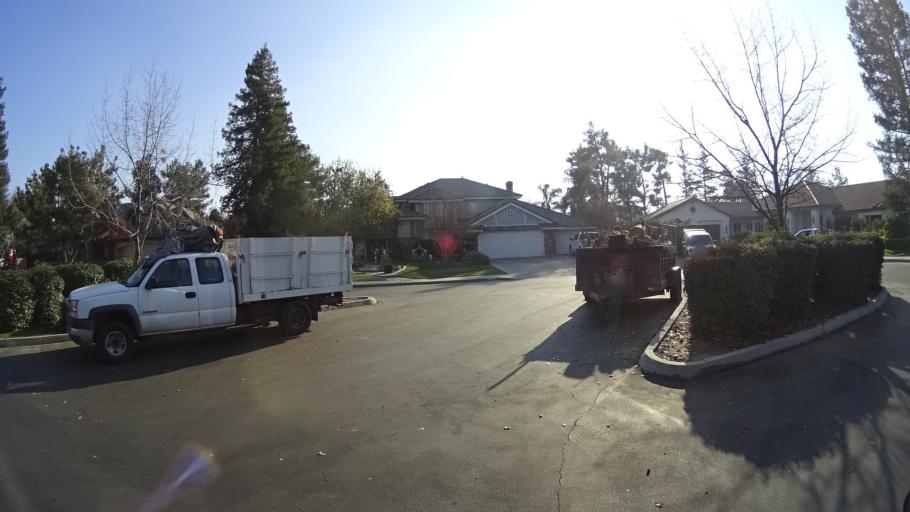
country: US
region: California
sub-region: Kern County
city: Greenacres
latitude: 35.3324
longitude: -119.1013
